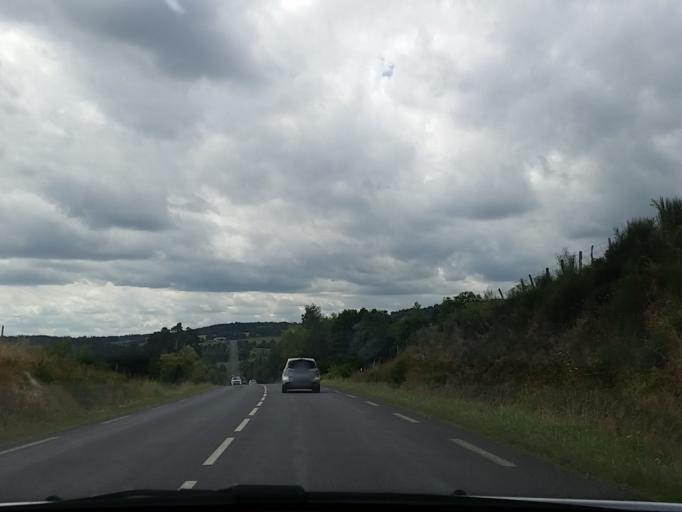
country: FR
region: Auvergne
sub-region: Departement du Cantal
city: Saint-Flour
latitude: 45.0176
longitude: 3.0558
